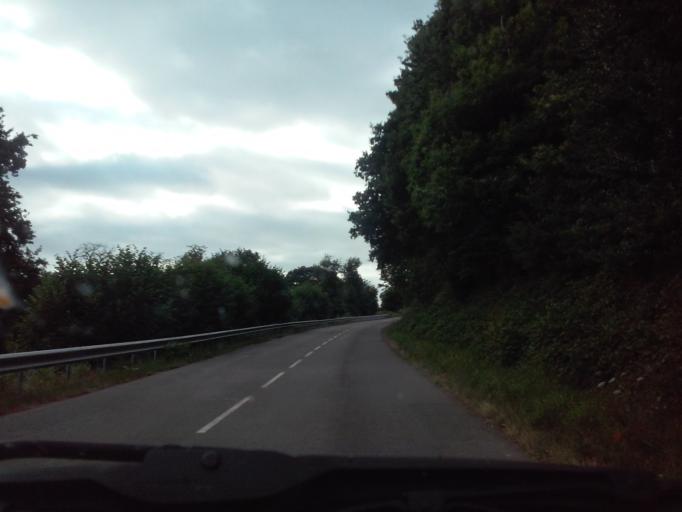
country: FR
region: Brittany
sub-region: Departement d'Ille-et-Vilaine
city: Saint-Senoux
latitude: 47.9080
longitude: -1.7914
